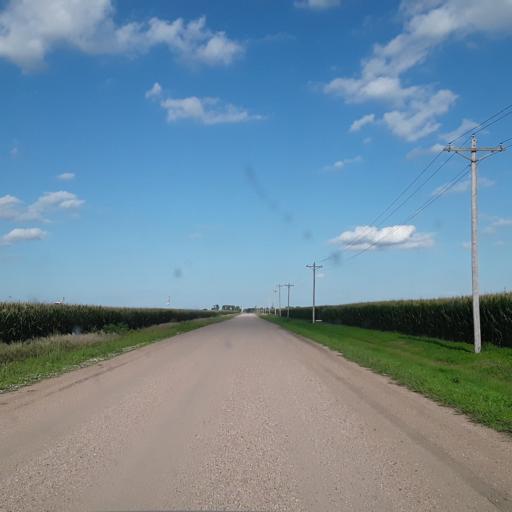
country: US
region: Nebraska
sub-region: Hall County
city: Wood River
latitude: 40.9168
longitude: -98.5824
